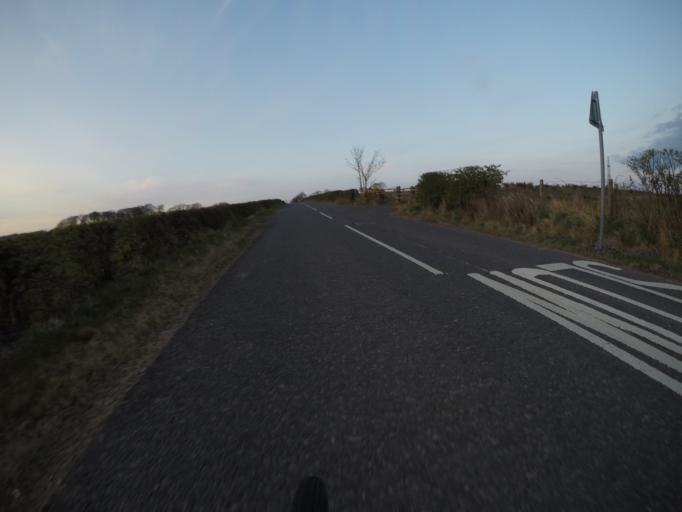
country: GB
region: Scotland
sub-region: South Ayrshire
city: Dundonald
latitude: 55.5596
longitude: -4.6101
